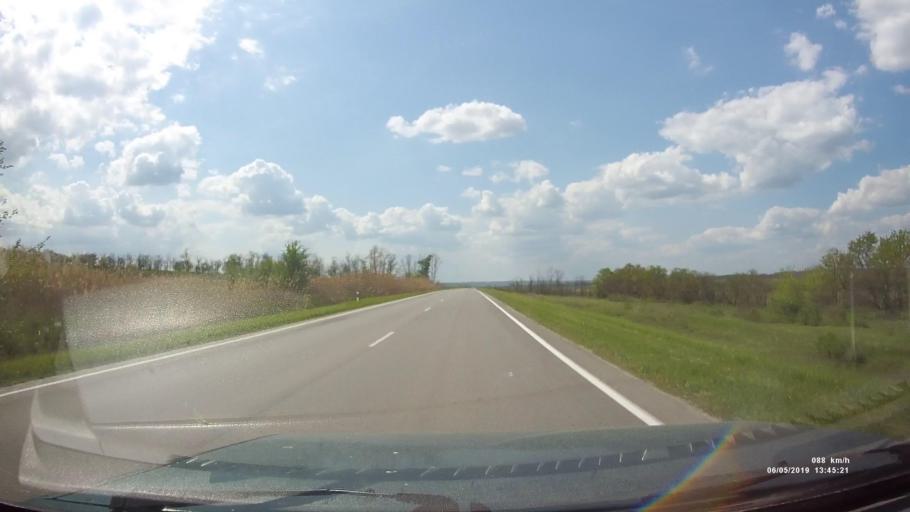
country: RU
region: Rostov
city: Melikhovskaya
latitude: 47.6571
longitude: 40.6024
